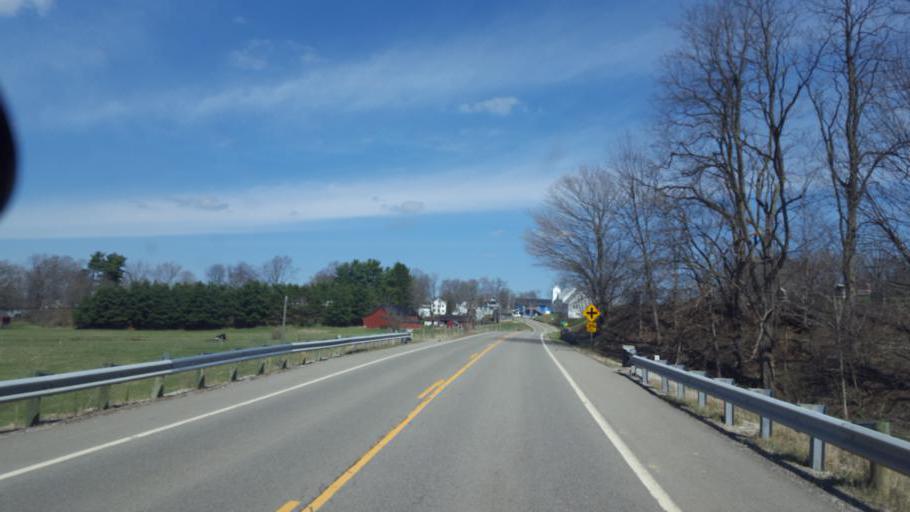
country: US
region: Ohio
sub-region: Ashland County
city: Ashland
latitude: 40.8833
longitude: -82.4293
